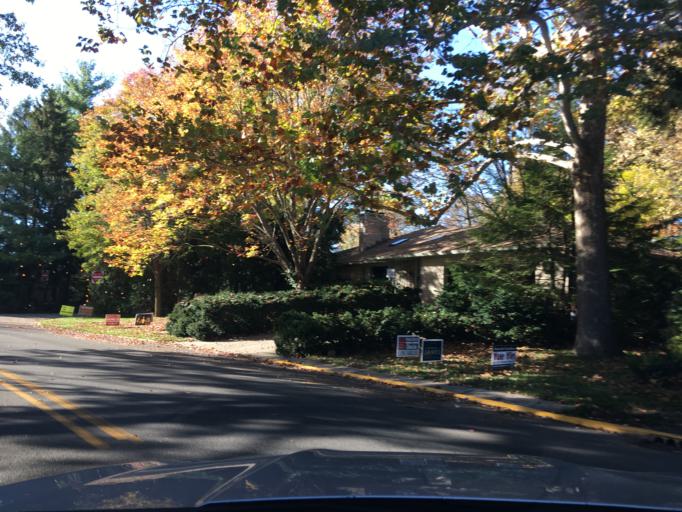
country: US
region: Indiana
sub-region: Tippecanoe County
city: West Lafayette
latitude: 40.4352
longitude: -86.9083
